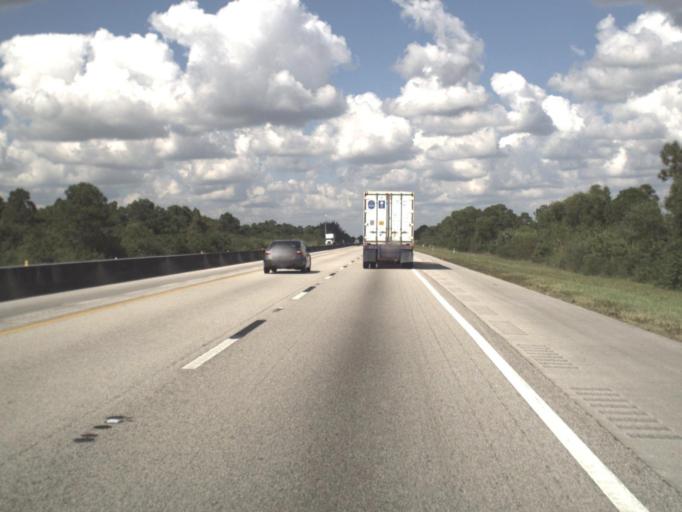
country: US
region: Florida
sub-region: Palm Beach County
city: Tequesta
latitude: 26.9963
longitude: -80.1980
